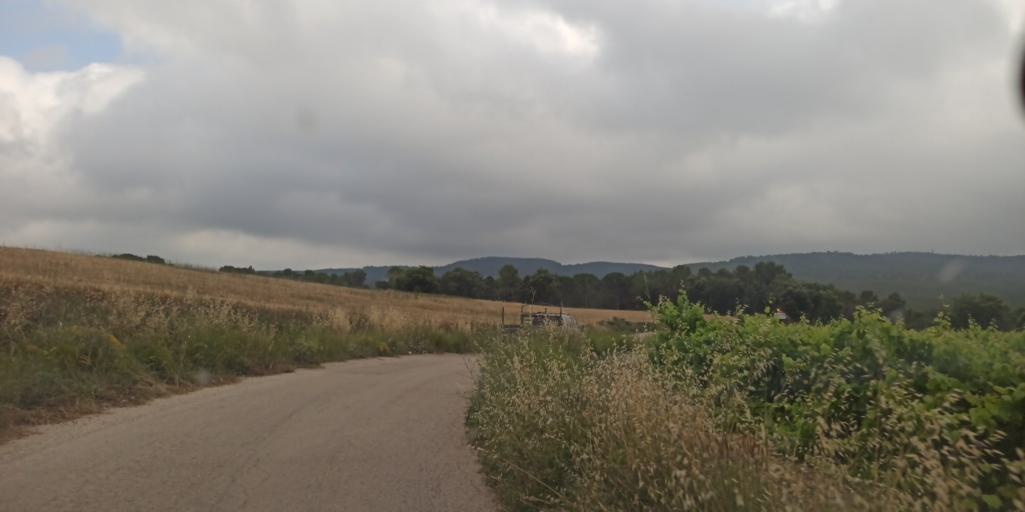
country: ES
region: Catalonia
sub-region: Provincia de Tarragona
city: Querol
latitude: 41.4241
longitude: 1.5004
